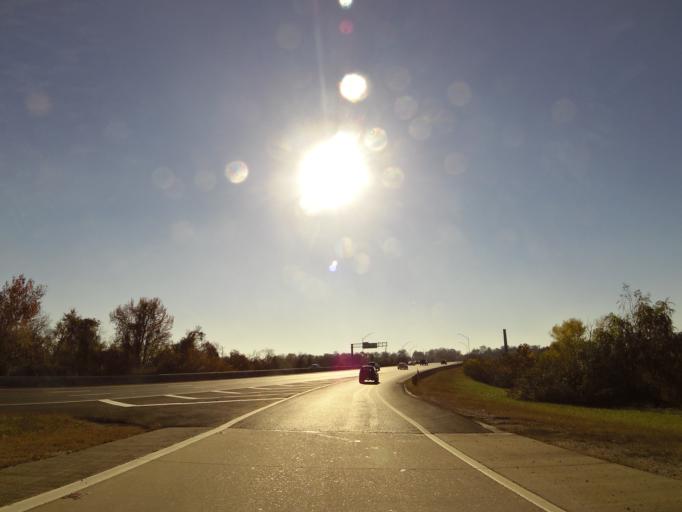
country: US
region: Tennessee
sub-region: Knox County
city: Knoxville
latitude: 35.9900
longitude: -83.9513
